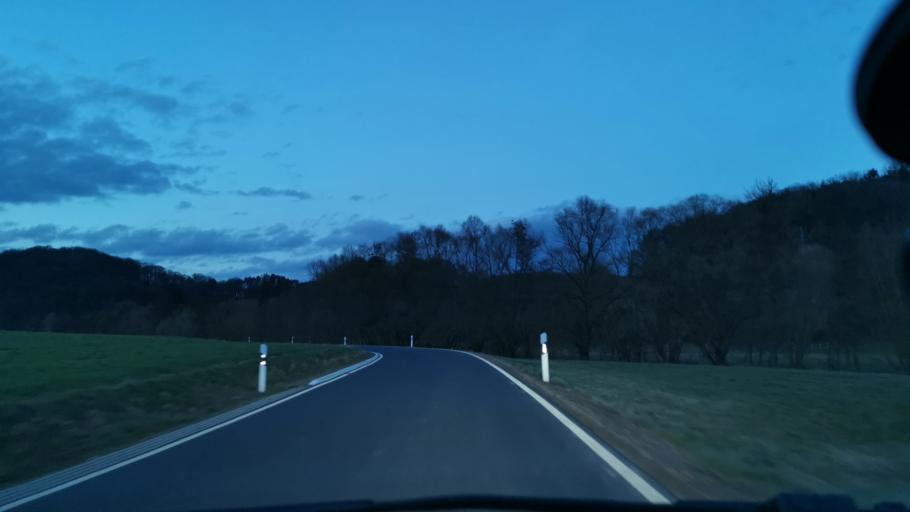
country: DE
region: Hesse
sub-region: Regierungsbezirk Kassel
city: Cornberg
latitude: 51.0608
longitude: 9.8335
